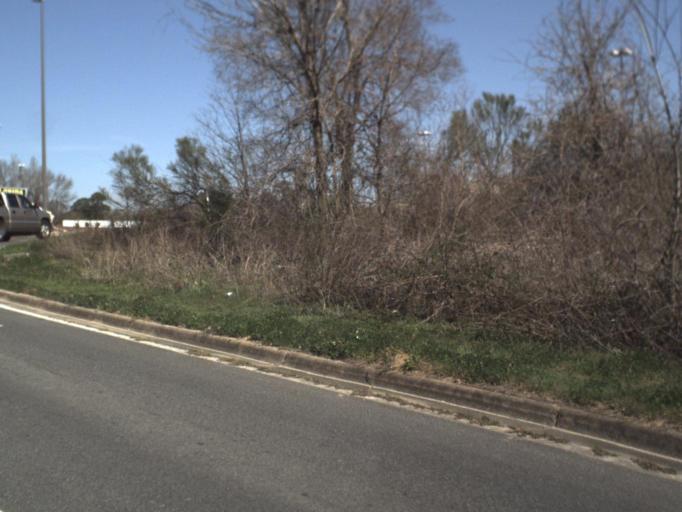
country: US
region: Florida
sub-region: Jackson County
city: Marianna
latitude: 30.7665
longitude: -85.2028
